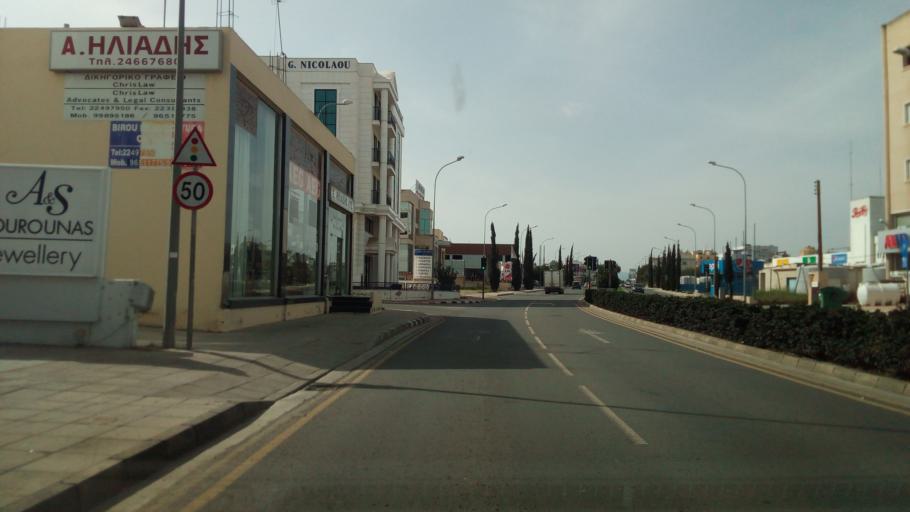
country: CY
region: Lefkosia
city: Nicosia
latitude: 35.1356
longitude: 33.3316
